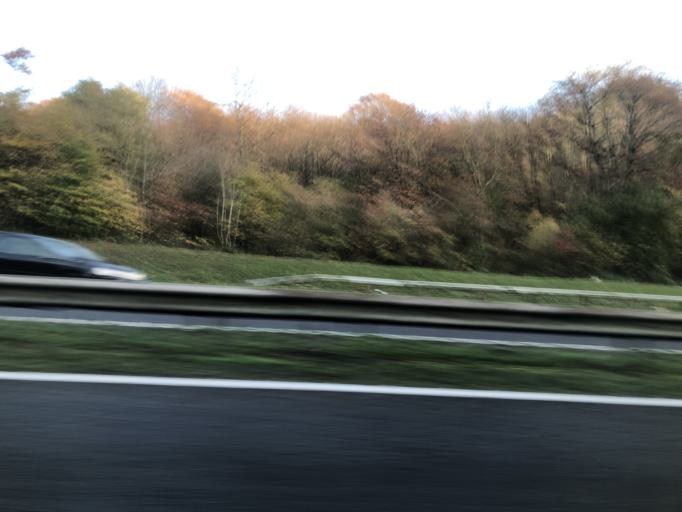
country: GB
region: England
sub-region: Kent
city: Shoreham
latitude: 51.3261
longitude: 0.1595
